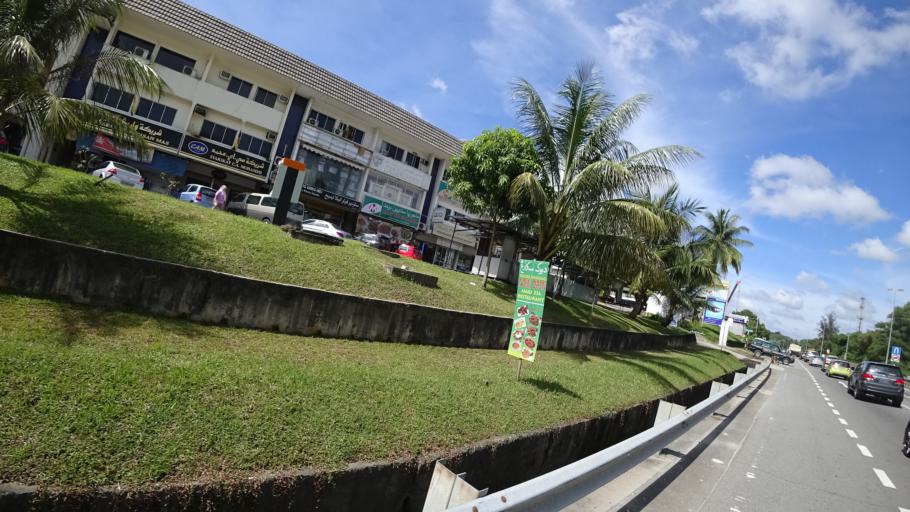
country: BN
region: Brunei and Muara
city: Bandar Seri Begawan
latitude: 4.8583
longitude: 114.8941
